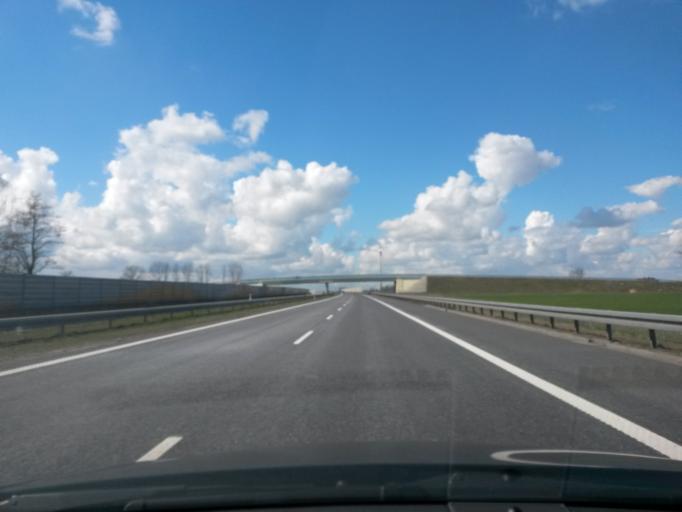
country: PL
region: Lodz Voivodeship
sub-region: Powiat poddebicki
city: Wartkowice
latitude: 52.0090
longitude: 18.9750
